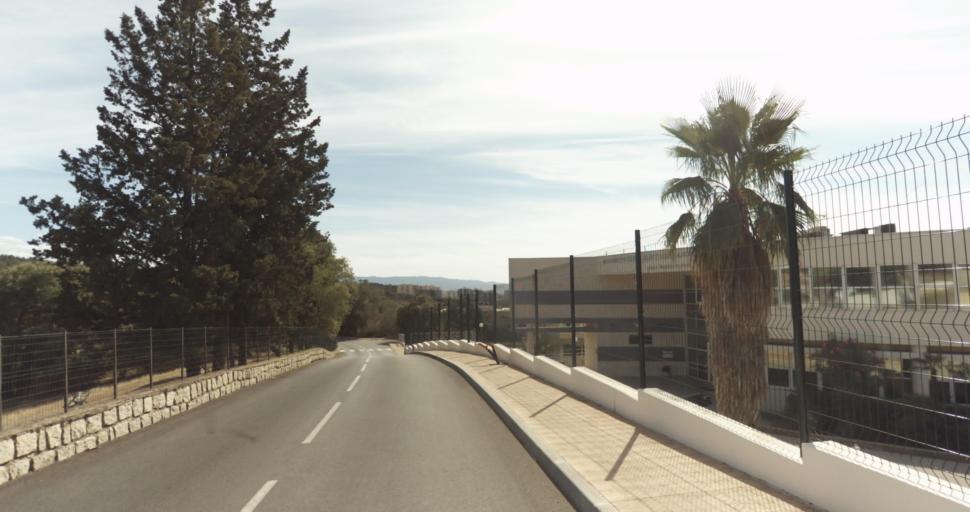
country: FR
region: Corsica
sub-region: Departement de la Corse-du-Sud
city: Ajaccio
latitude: 41.9484
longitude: 8.7574
